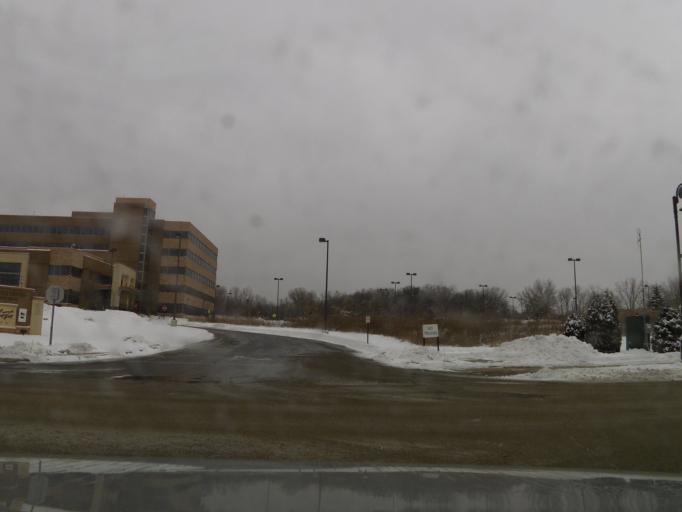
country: US
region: Minnesota
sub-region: Dakota County
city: West Saint Paul
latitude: 44.8836
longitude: -93.0856
